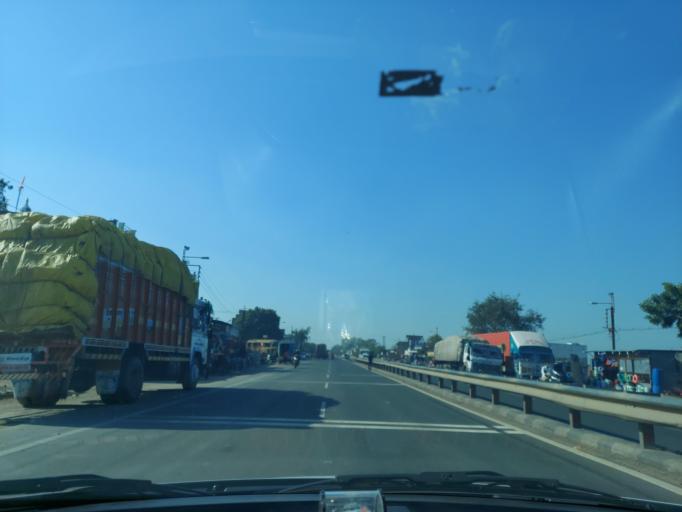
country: IN
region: Madhya Pradesh
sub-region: Dhar
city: Dhar
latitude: 22.7912
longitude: 75.2973
